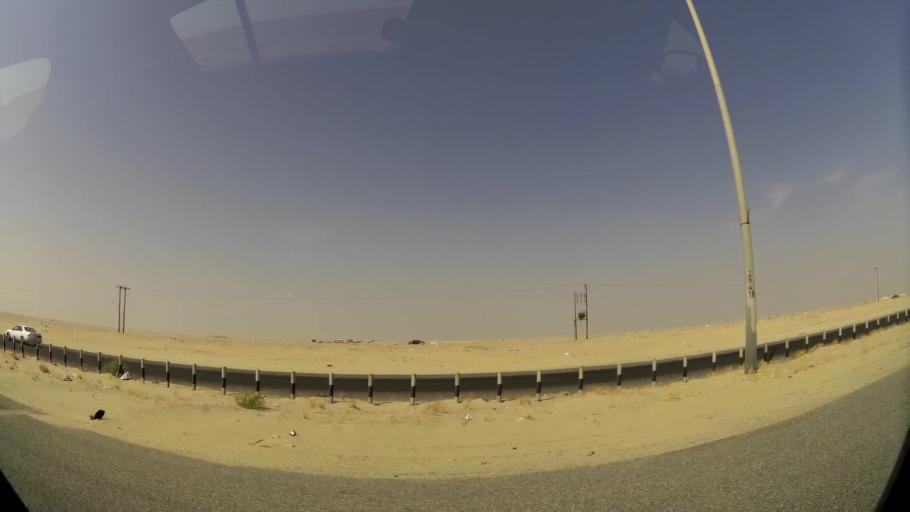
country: KW
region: Al Ahmadi
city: Al Wafrah
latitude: 28.8271
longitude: 48.0518
